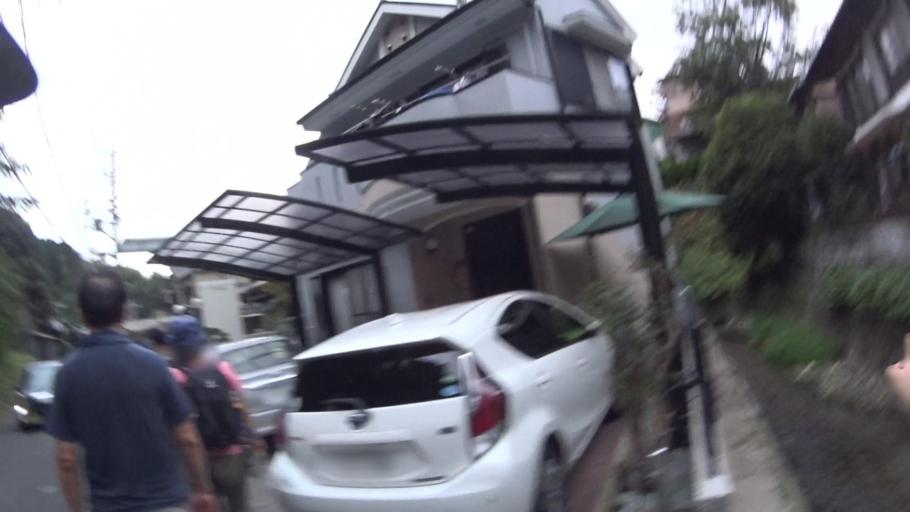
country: JP
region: Osaka
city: Kaizuka
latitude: 34.4583
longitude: 135.2908
